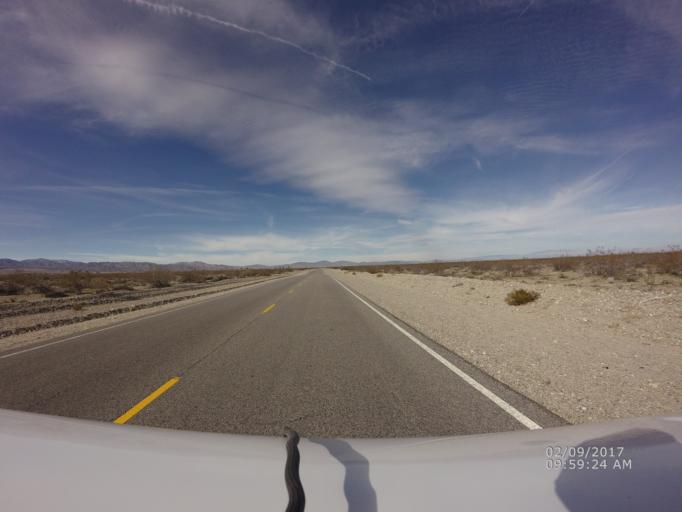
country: US
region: California
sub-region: Los Angeles County
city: Lake Los Angeles
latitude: 34.5427
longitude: -117.8720
